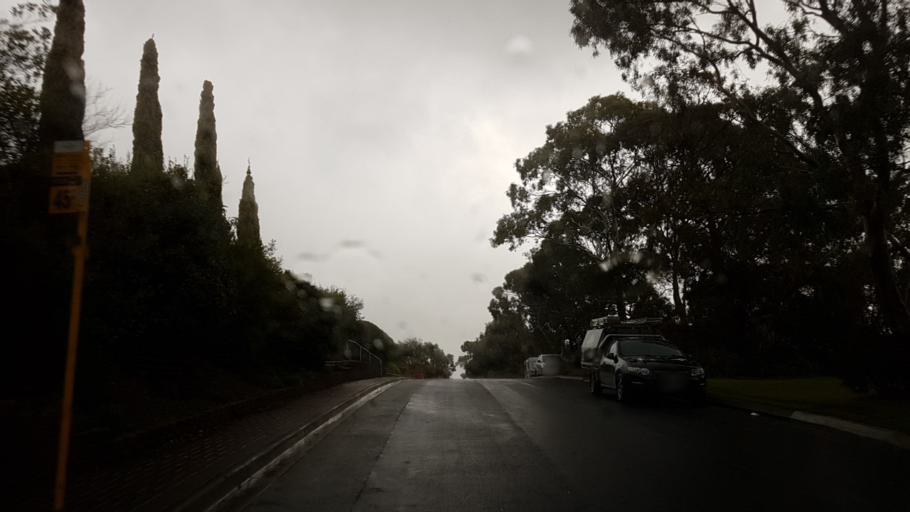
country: AU
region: South Australia
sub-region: Onkaparinga
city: Craigburn Farm
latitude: -35.0913
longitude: 138.5922
